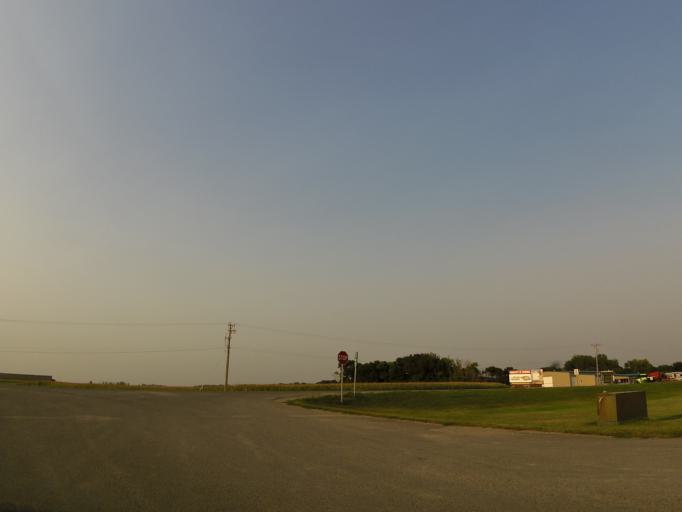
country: US
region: North Dakota
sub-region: Traill County
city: Mayville
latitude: 47.4978
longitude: -97.3118
